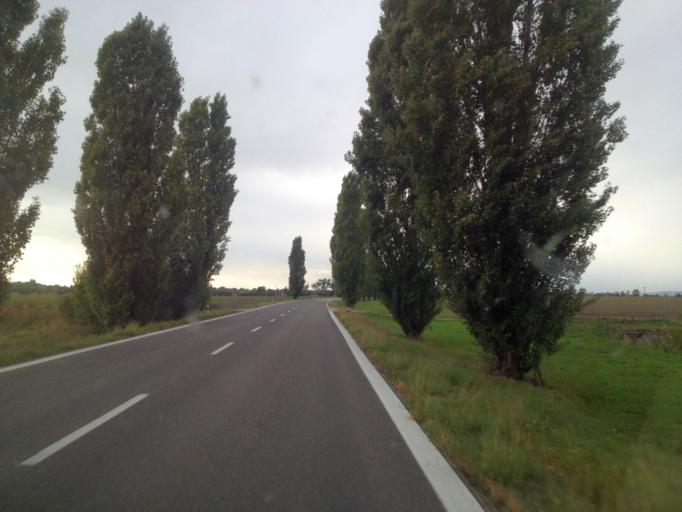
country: HU
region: Komarom-Esztergom
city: Labatlan
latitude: 47.7626
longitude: 18.5062
